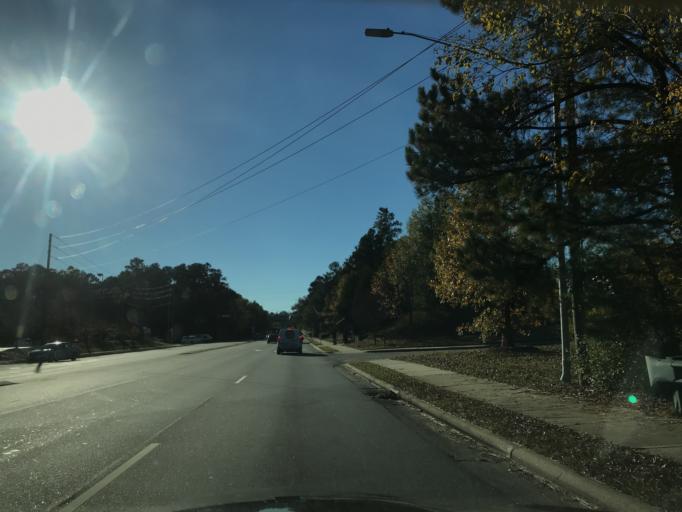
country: US
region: North Carolina
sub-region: Wake County
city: Raleigh
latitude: 35.7704
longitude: -78.6130
